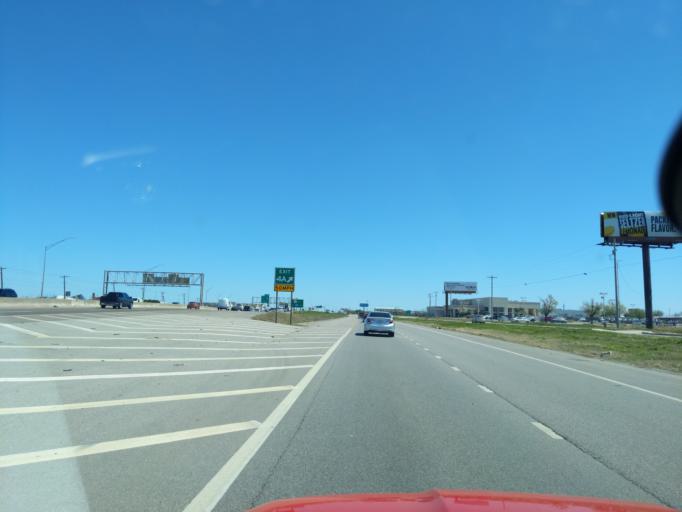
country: US
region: Oklahoma
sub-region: Cleveland County
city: Moore
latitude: 35.3918
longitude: -97.5026
